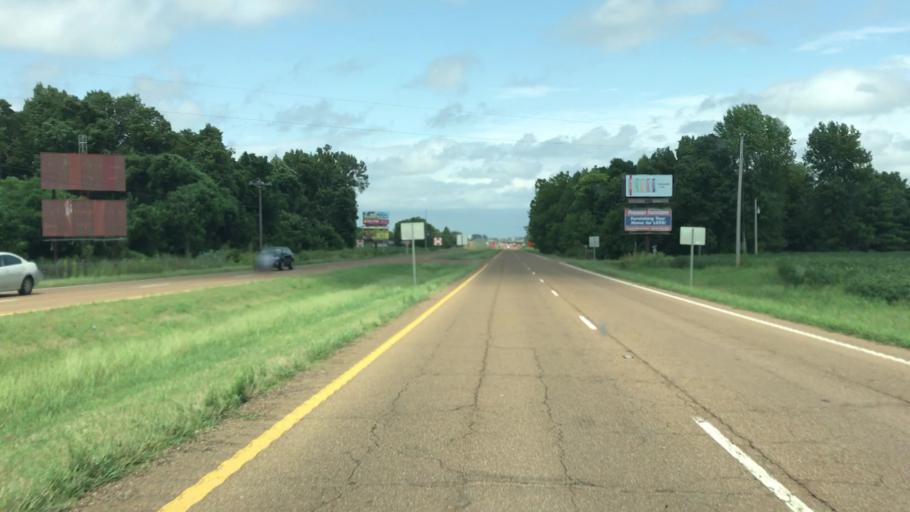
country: US
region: Tennessee
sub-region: Obion County
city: Englewood
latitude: 36.3850
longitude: -89.1073
